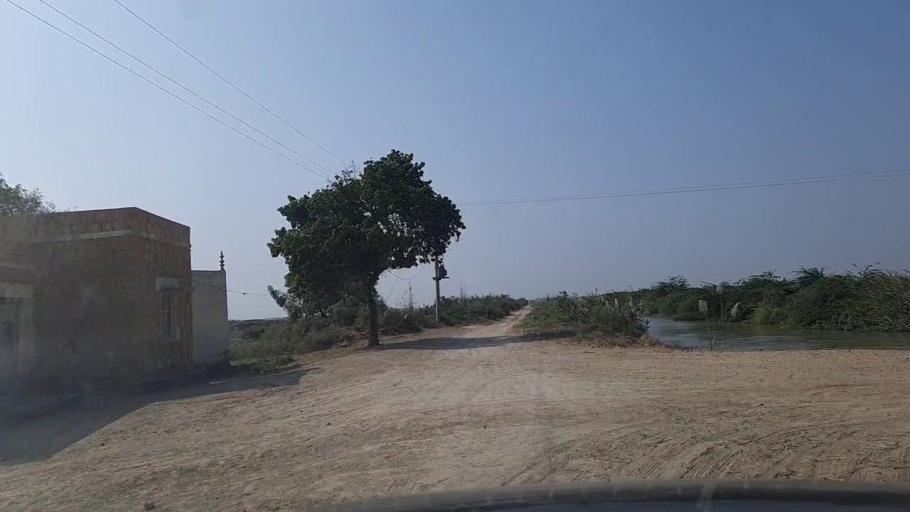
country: PK
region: Sindh
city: Gharo
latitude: 24.7202
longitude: 67.6652
